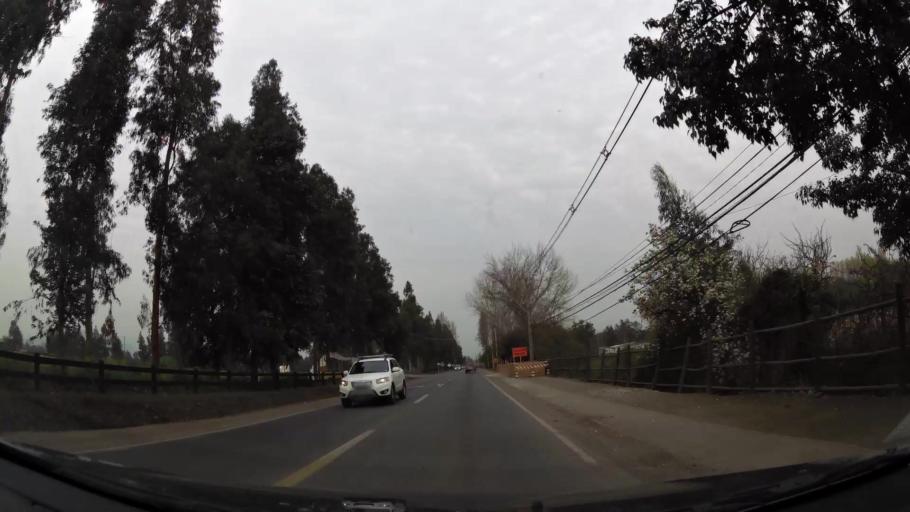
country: CL
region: Santiago Metropolitan
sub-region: Provincia de Chacabuco
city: Chicureo Abajo
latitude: -33.2856
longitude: -70.6900
